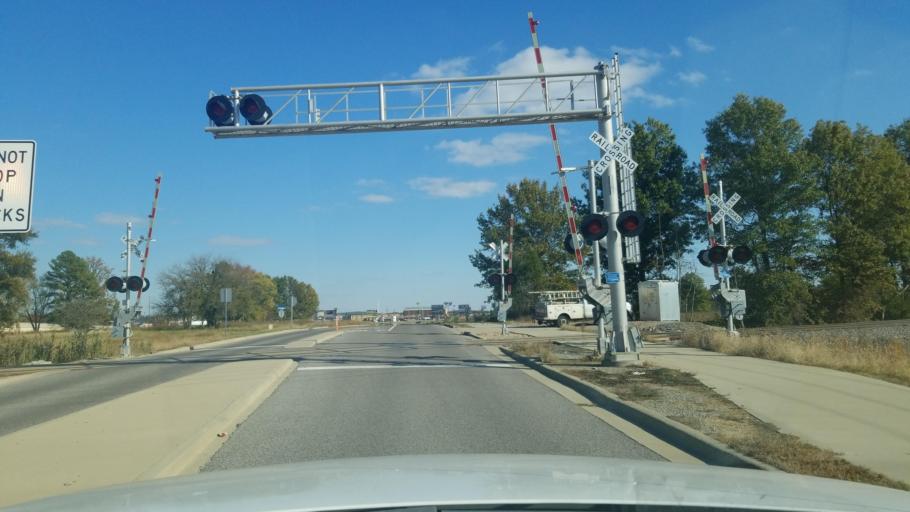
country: US
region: Illinois
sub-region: Williamson County
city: Marion
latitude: 37.7433
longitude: -88.9795
